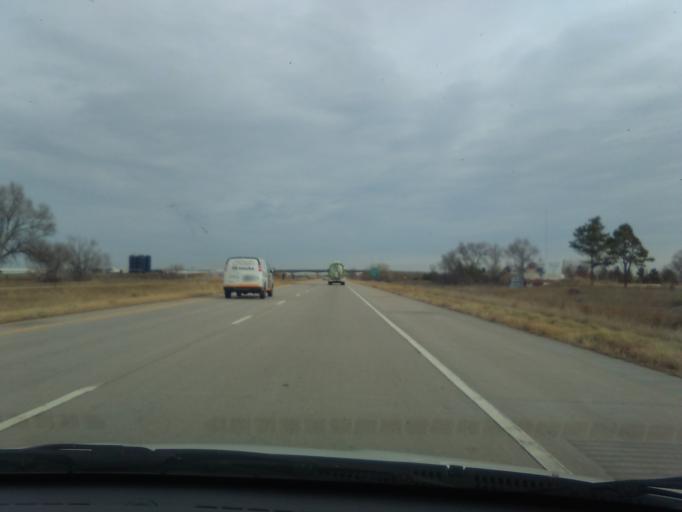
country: US
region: Colorado
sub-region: Morgan County
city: Fort Morgan
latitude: 40.2362
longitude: -104.0796
